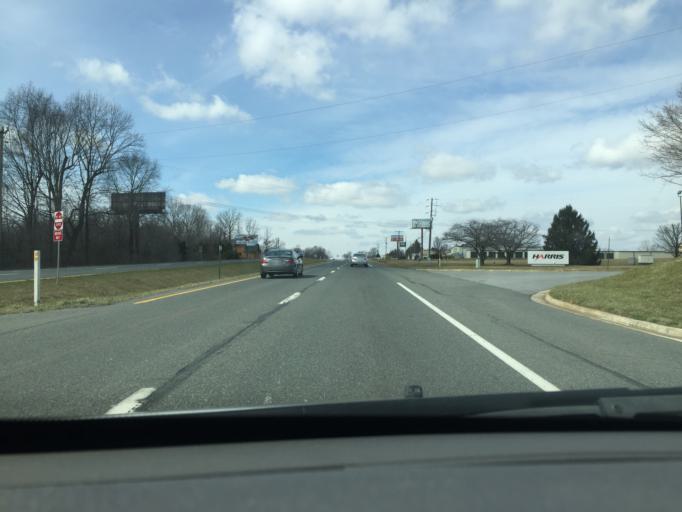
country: US
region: Virginia
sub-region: Campbell County
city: Timberlake
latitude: 37.3053
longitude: -79.2964
